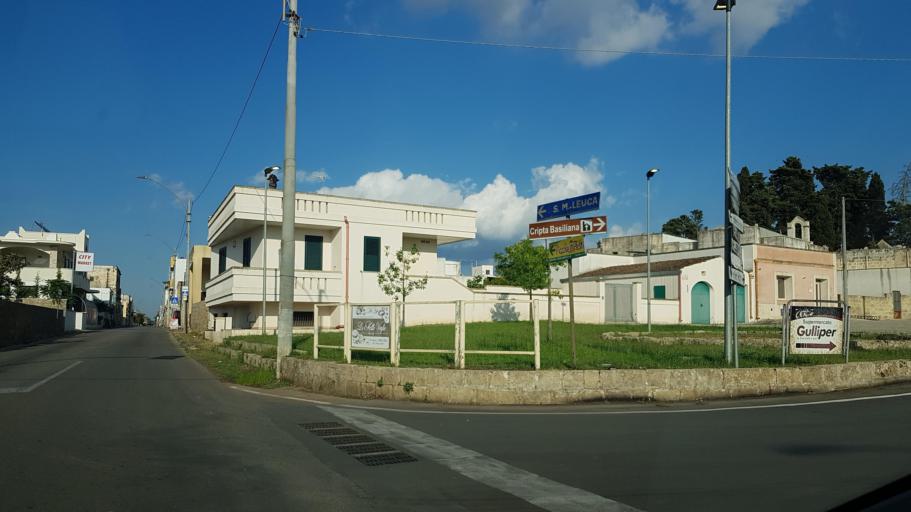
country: IT
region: Apulia
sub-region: Provincia di Lecce
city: Miggiano
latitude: 39.9650
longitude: 18.3051
